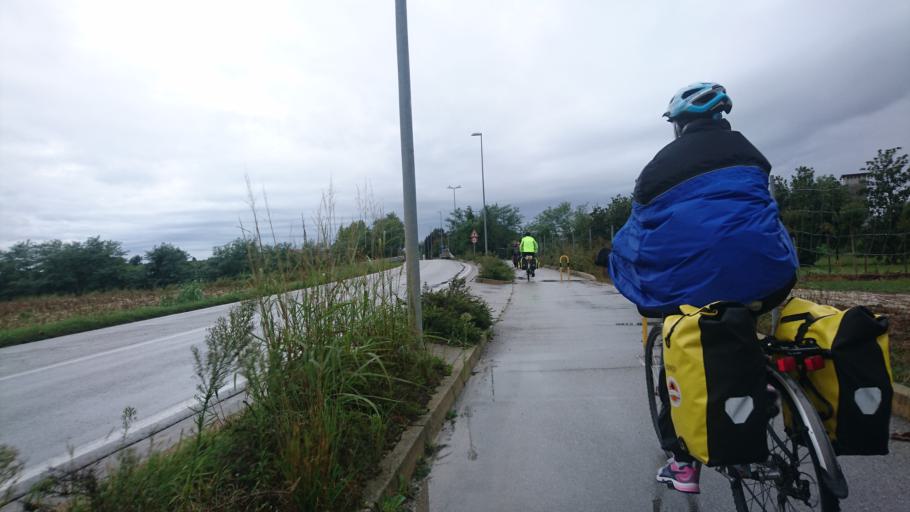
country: IT
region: Veneto
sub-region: Provincia di Treviso
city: Loria Bessica
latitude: 45.7350
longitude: 11.8751
